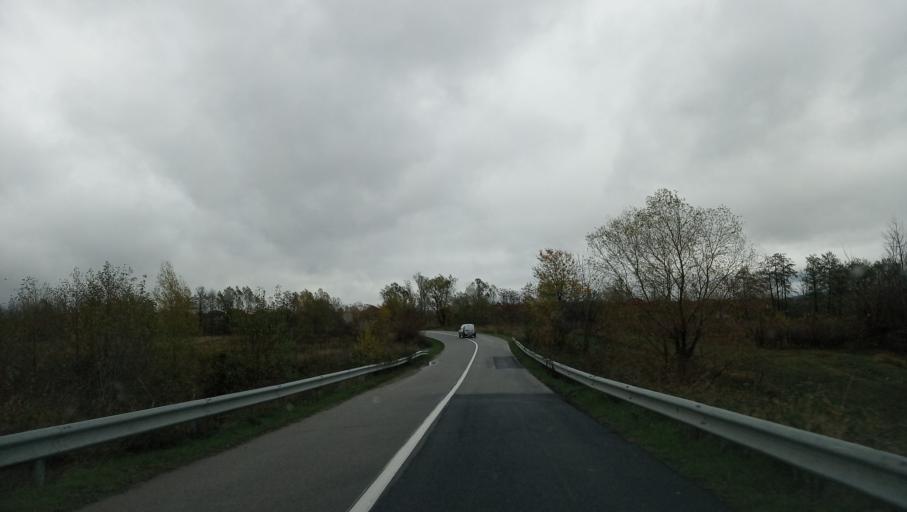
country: RO
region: Gorj
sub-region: Comuna Musetesti
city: Musetesti
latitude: 45.1662
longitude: 23.4785
